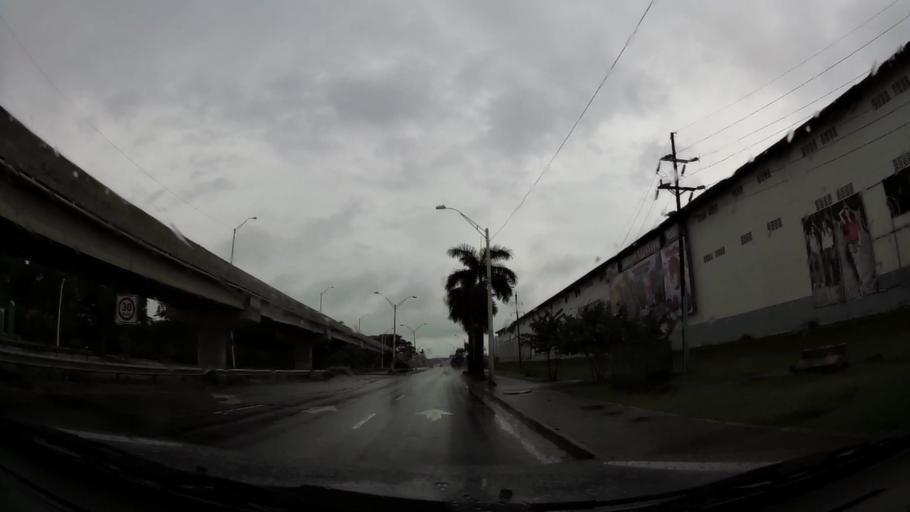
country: PA
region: Colon
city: Arco Iris
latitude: 9.3402
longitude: -79.8875
